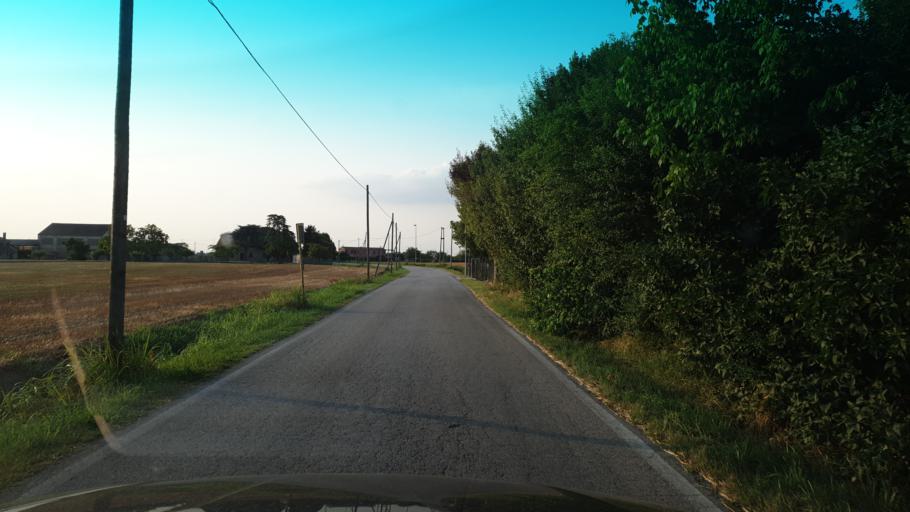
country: IT
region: Veneto
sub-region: Provincia di Rovigo
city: Castelguglielmo
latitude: 45.0089
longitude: 11.5263
